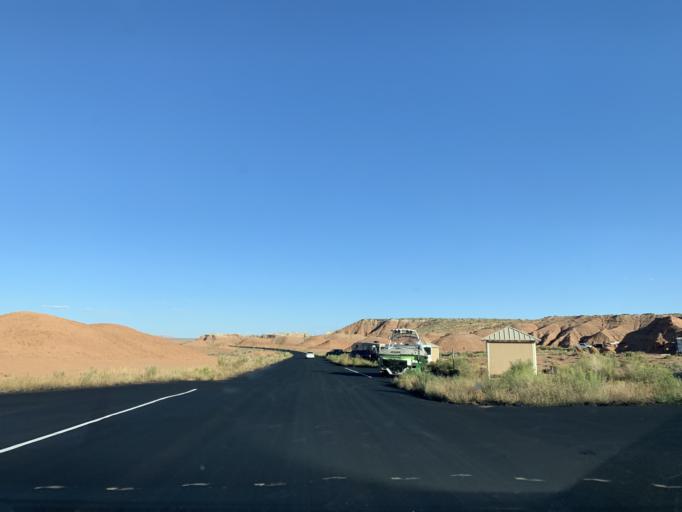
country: US
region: Utah
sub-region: Emery County
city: Ferron
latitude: 38.5733
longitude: -110.7134
